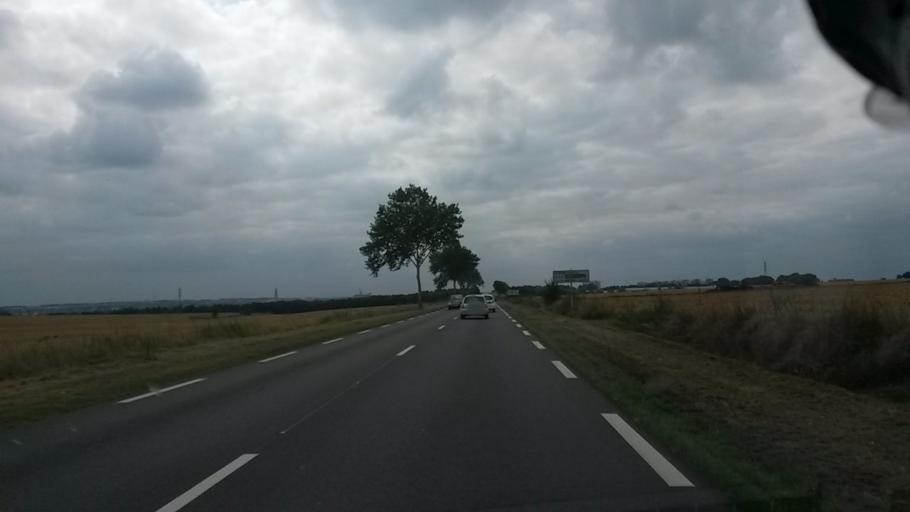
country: FR
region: Picardie
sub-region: Departement de la Somme
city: Camon
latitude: 49.9169
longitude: 2.3544
